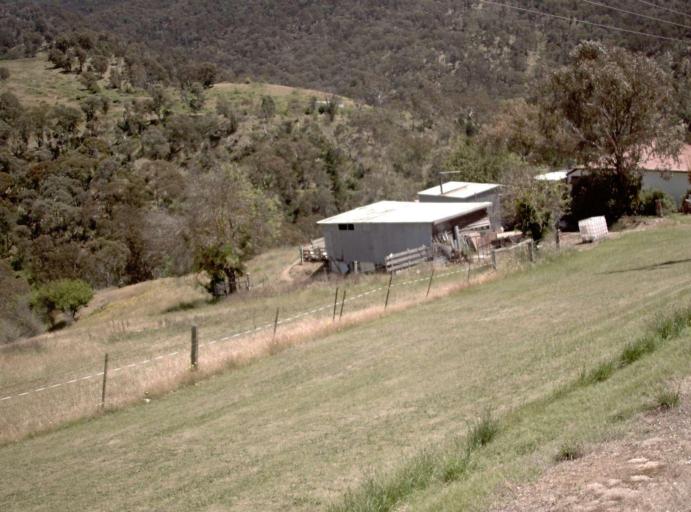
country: AU
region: Victoria
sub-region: Alpine
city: Mount Beauty
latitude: -37.1047
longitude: 147.5818
